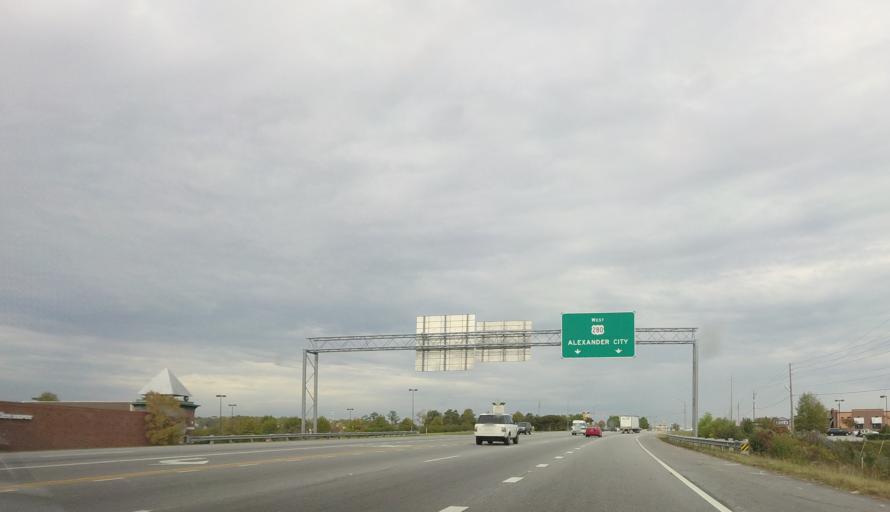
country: US
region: Alabama
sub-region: Lee County
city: Opelika
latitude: 32.6188
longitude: -85.4032
